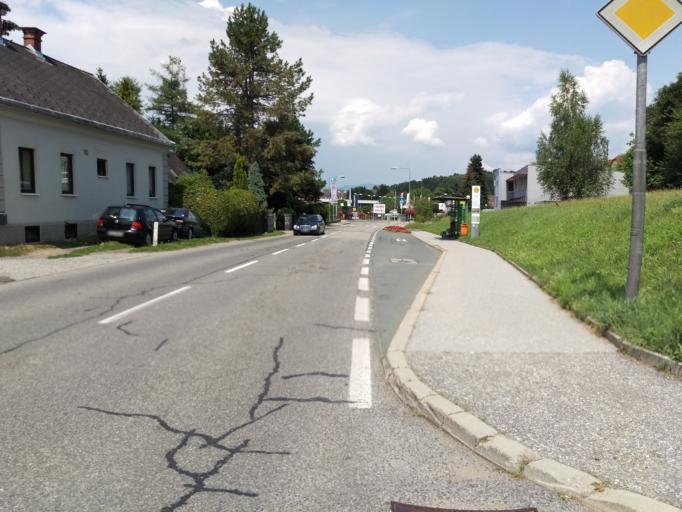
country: AT
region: Styria
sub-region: Politischer Bezirk Graz-Umgebung
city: Raaba
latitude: 47.0303
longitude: 15.4953
